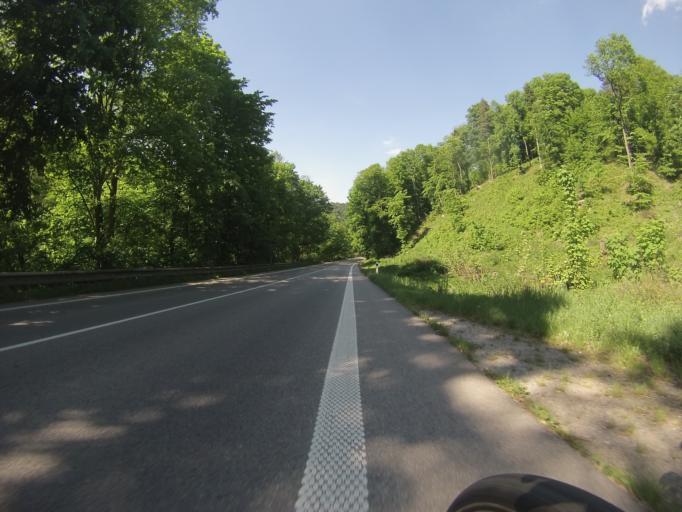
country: CZ
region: South Moravian
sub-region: Okres Blansko
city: Adamov
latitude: 49.3283
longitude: 16.6433
